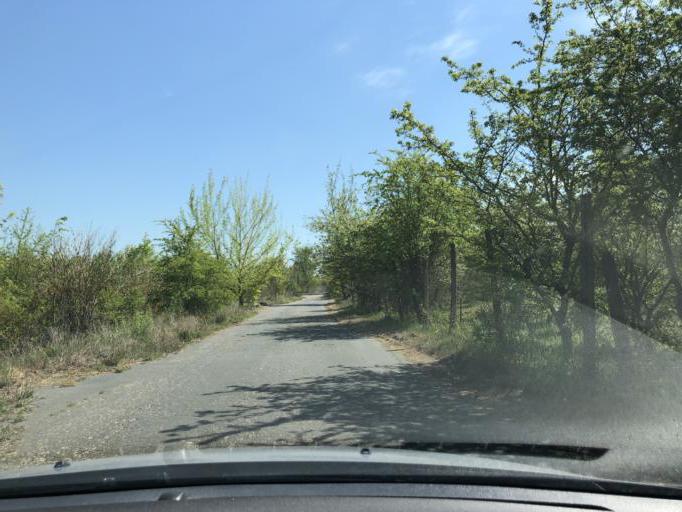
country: DE
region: Saxony-Anhalt
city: Dieskau
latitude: 51.4452
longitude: 11.9998
